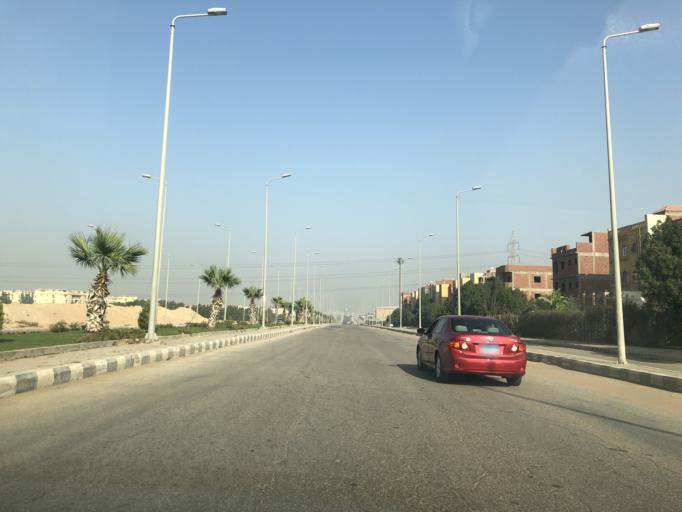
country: EG
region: Al Jizah
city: Madinat Sittah Uktubar
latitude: 29.9474
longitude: 31.0660
